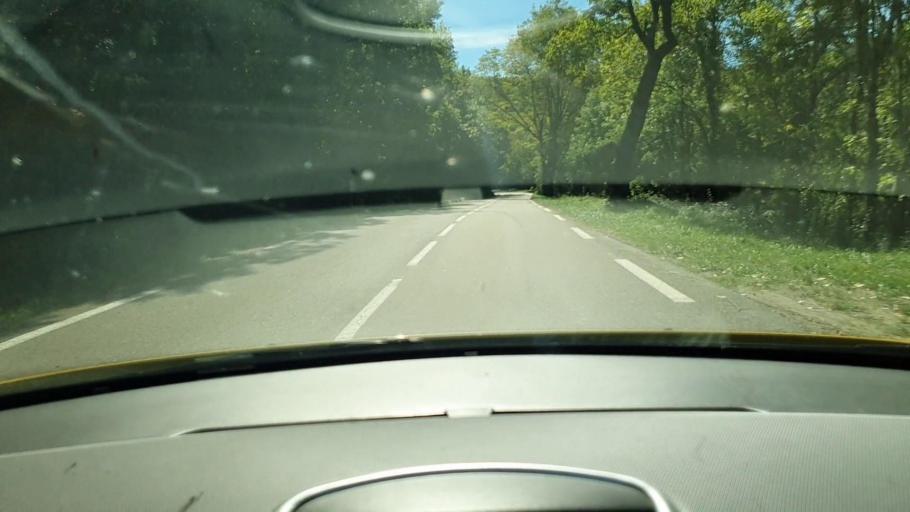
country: FR
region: Languedoc-Roussillon
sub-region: Departement du Gard
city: Le Vigan
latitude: 43.9719
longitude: 3.4147
